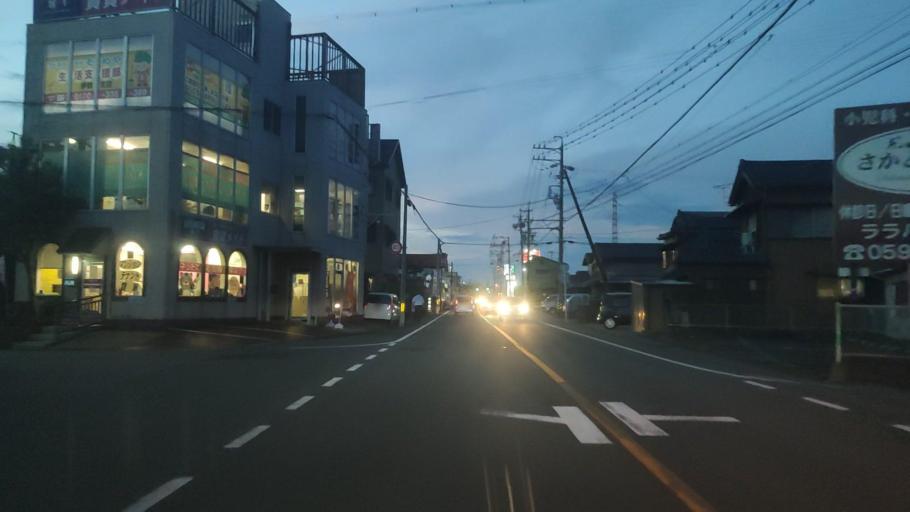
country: JP
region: Mie
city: Ise
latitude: 34.5033
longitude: 136.7172
